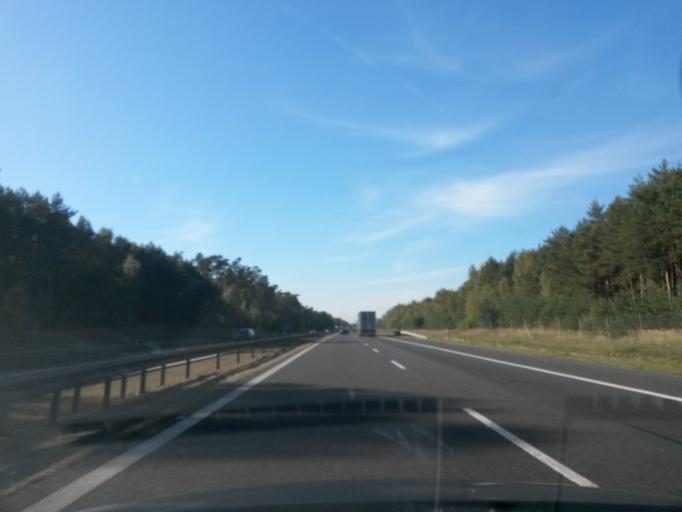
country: PL
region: Opole Voivodeship
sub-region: Powiat opolski
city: Niemodlin
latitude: 50.6715
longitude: 17.6664
